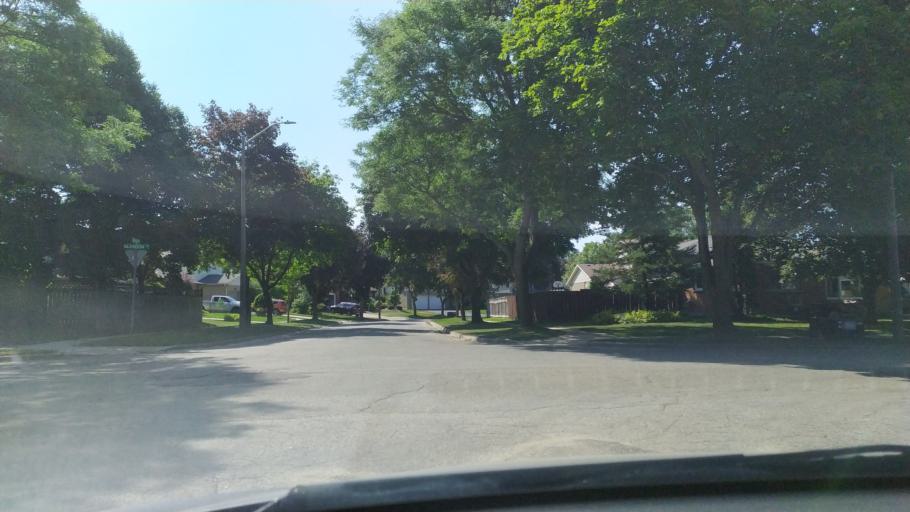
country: CA
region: Ontario
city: Stratford
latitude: 43.3828
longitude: -80.9667
